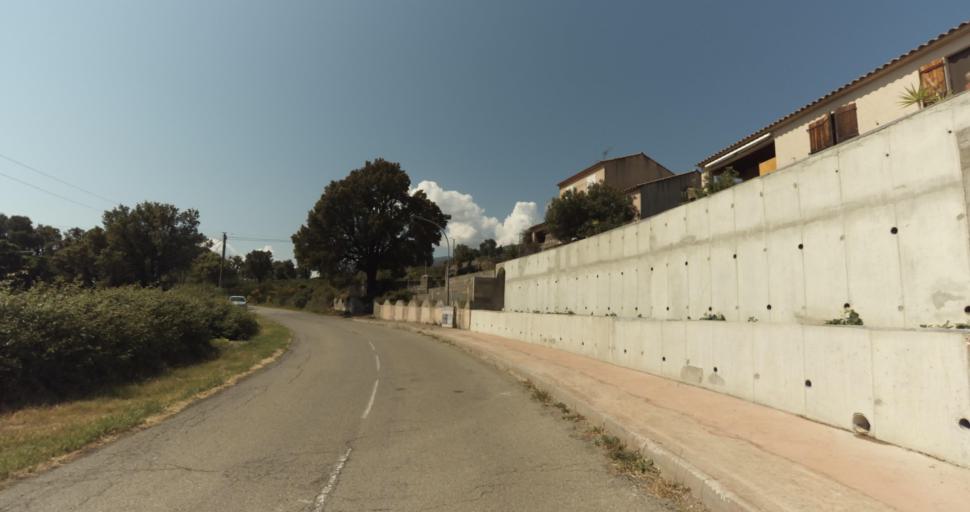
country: FR
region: Corsica
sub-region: Departement de la Haute-Corse
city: Biguglia
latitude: 42.6178
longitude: 9.4234
